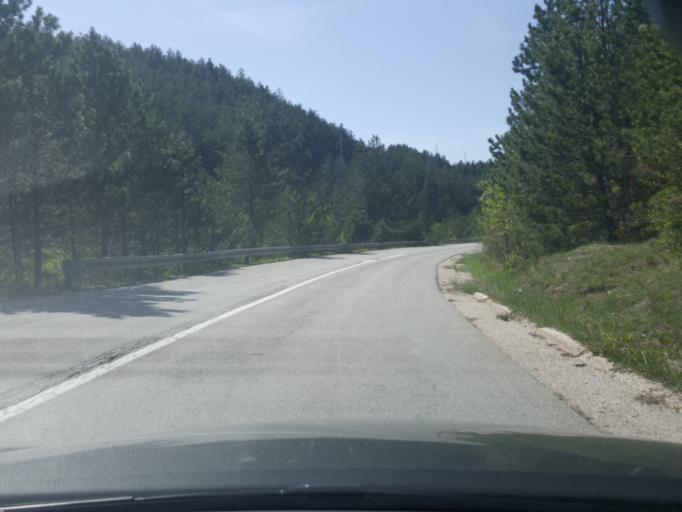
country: RS
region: Central Serbia
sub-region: Zlatiborski Okrug
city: Cajetina
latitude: 43.7861
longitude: 19.6663
